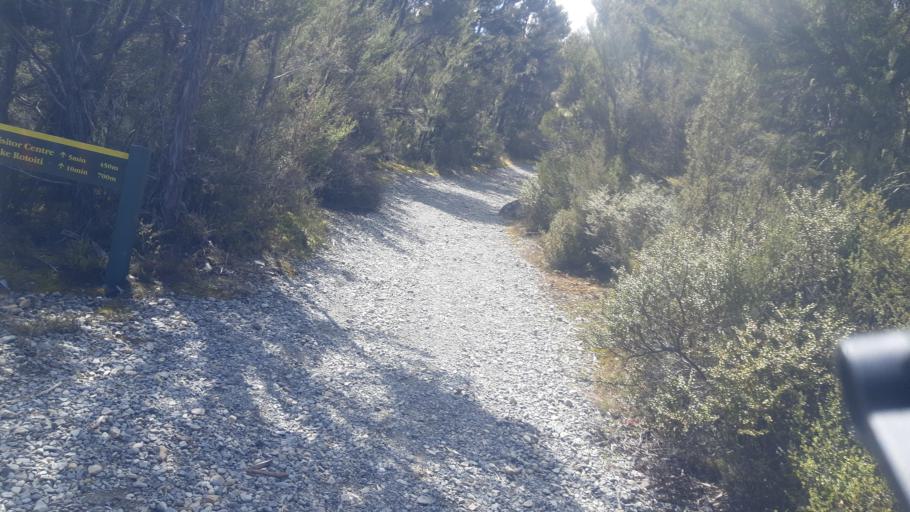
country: NZ
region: Tasman
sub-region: Tasman District
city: Wakefield
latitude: -41.8023
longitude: 172.8400
